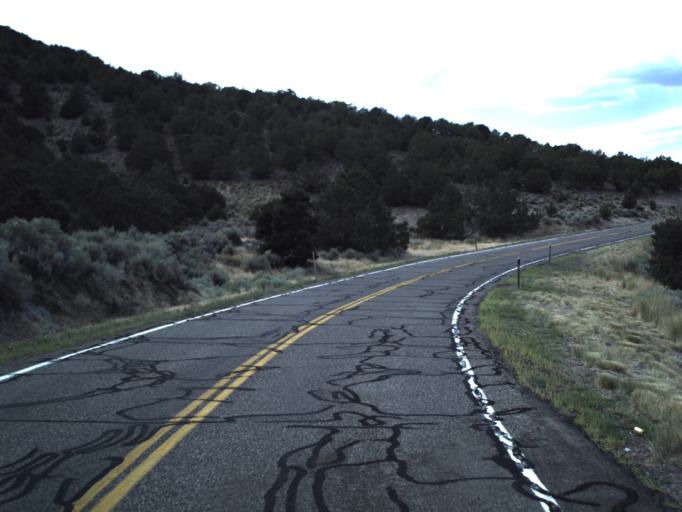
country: US
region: Utah
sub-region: Sevier County
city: Aurora
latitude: 38.7759
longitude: -111.9336
